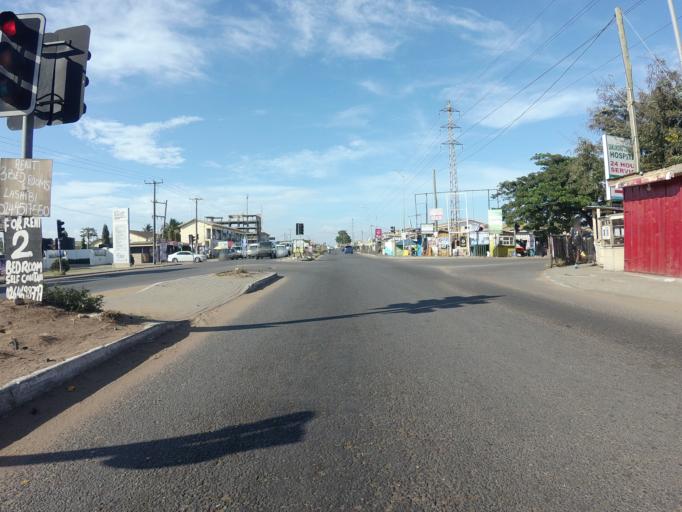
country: GH
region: Greater Accra
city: Nungua
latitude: 5.6239
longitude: -0.0692
